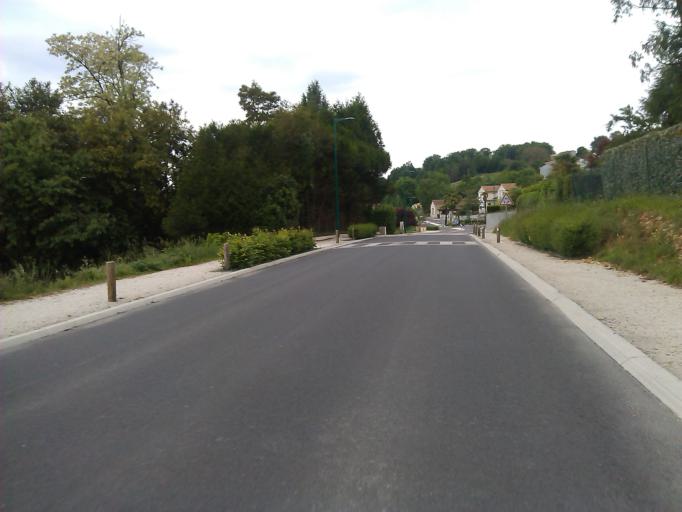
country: FR
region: Poitou-Charentes
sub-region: Departement de la Charente
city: Nersac
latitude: 45.6433
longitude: 0.0558
